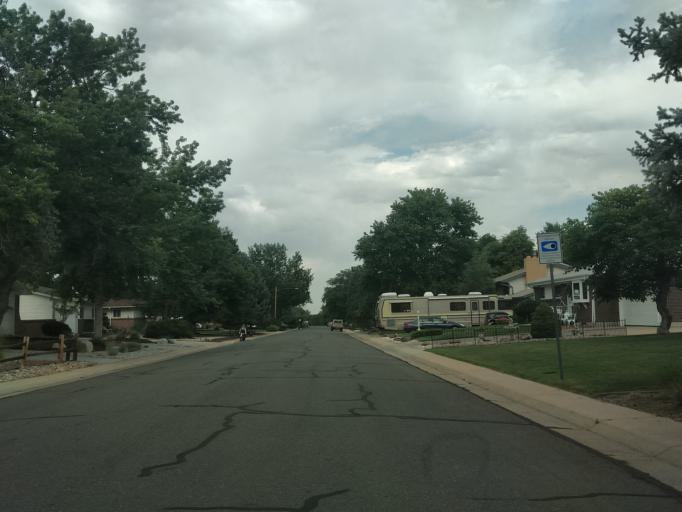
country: US
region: Colorado
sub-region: Jefferson County
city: Lakewood
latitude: 39.7001
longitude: -105.1037
